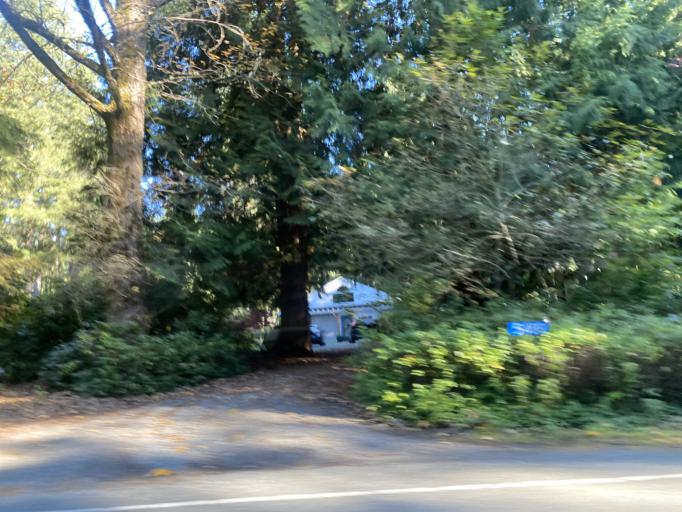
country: US
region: Washington
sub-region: Island County
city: Langley
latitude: 48.0111
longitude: -122.4261
